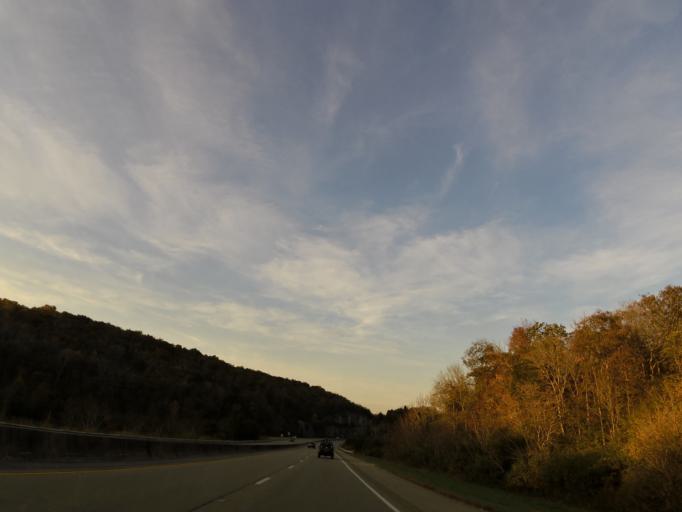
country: US
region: Kentucky
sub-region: Jessamine County
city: Wilmore
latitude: 37.7597
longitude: -84.6167
